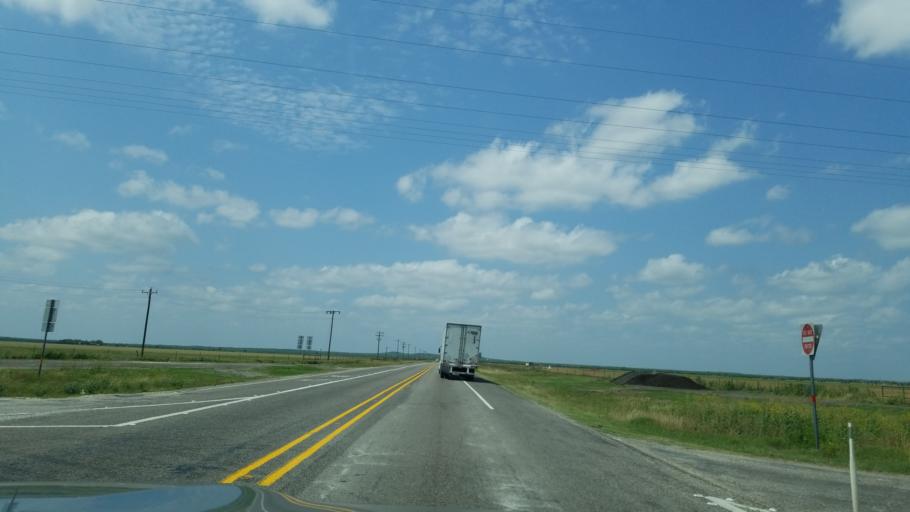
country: US
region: Texas
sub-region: Frio County
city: Pearsall
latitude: 28.9722
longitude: -99.2428
